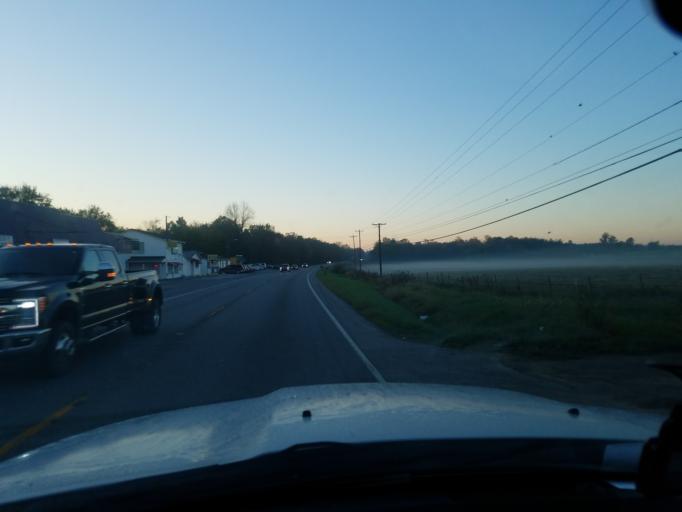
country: US
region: Kentucky
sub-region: Laurel County
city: London
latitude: 37.0843
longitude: -84.0608
